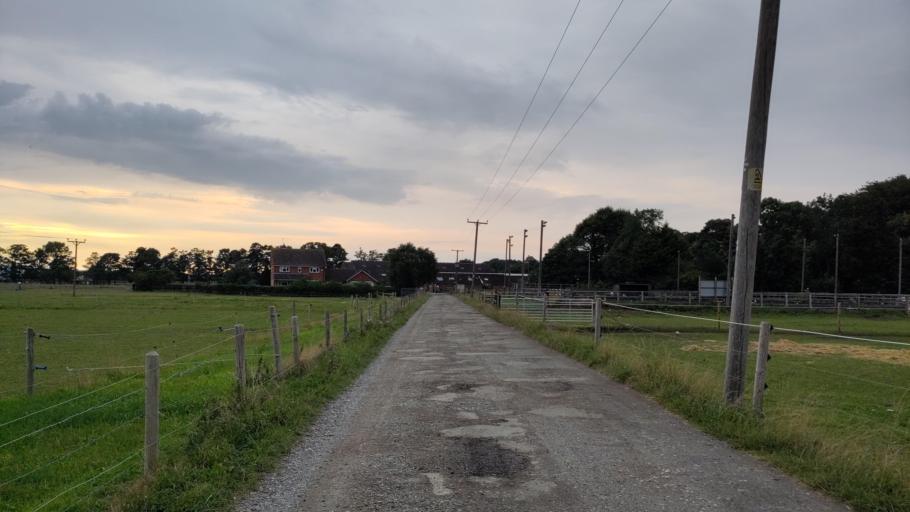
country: GB
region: England
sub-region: Cheshire West and Chester
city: Blacon
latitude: 53.1925
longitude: -2.9431
